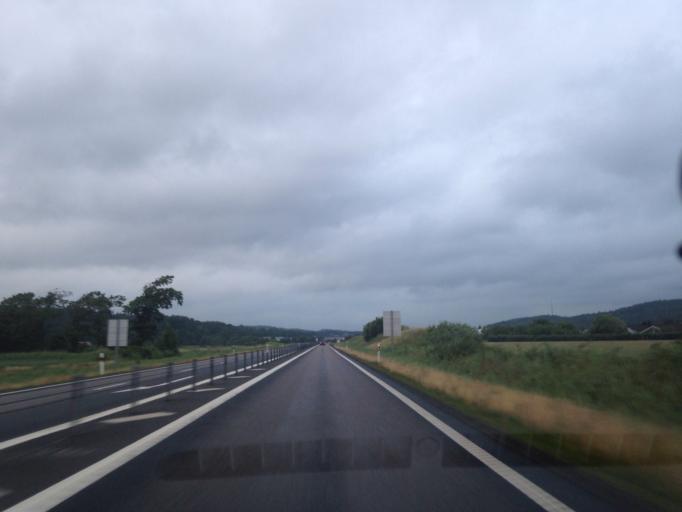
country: SE
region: Halland
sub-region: Varbergs Kommun
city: Varberg
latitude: 57.1571
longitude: 12.2712
